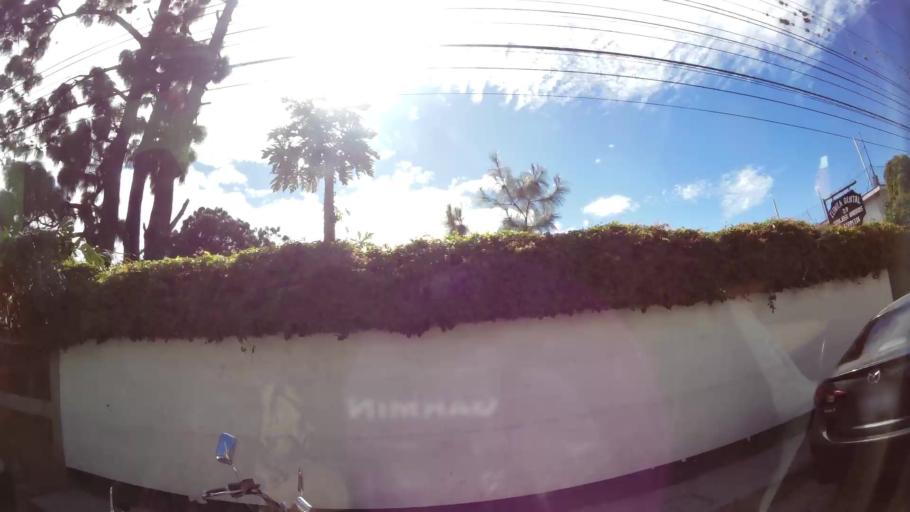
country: GT
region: Solola
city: Panajachel
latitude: 14.7411
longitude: -91.1582
